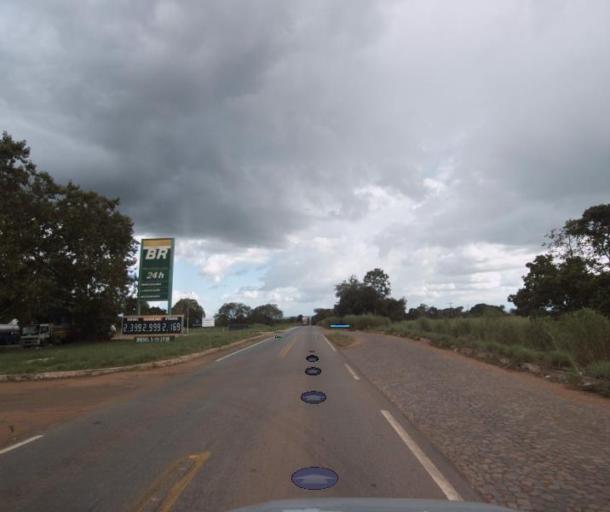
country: BR
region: Goias
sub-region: Porangatu
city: Porangatu
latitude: -13.3183
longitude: -49.1183
